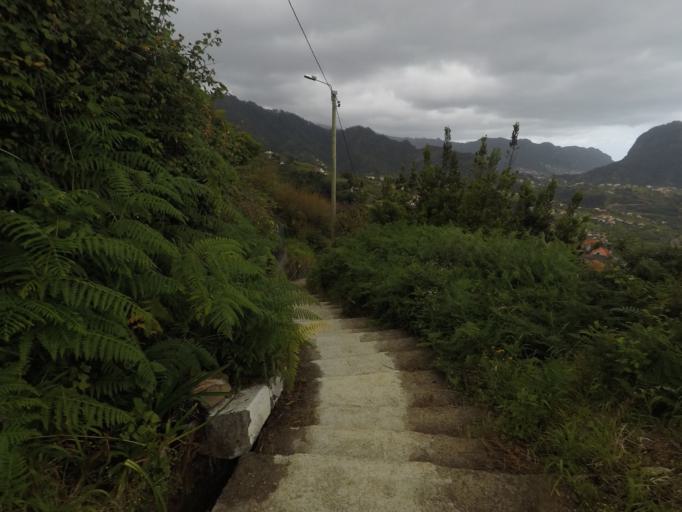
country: PT
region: Madeira
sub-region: Santa Cruz
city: Santa Cruz
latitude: 32.7519
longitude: -16.8257
